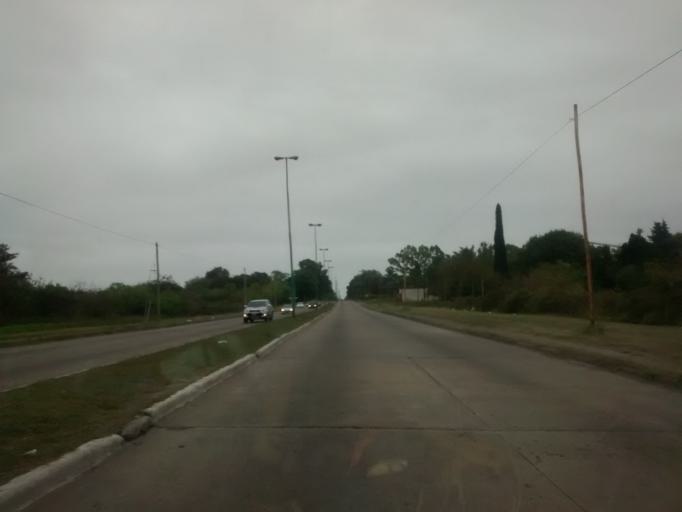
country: AR
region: Buenos Aires
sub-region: Partido de La Plata
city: La Plata
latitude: -34.9748
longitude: -58.0258
